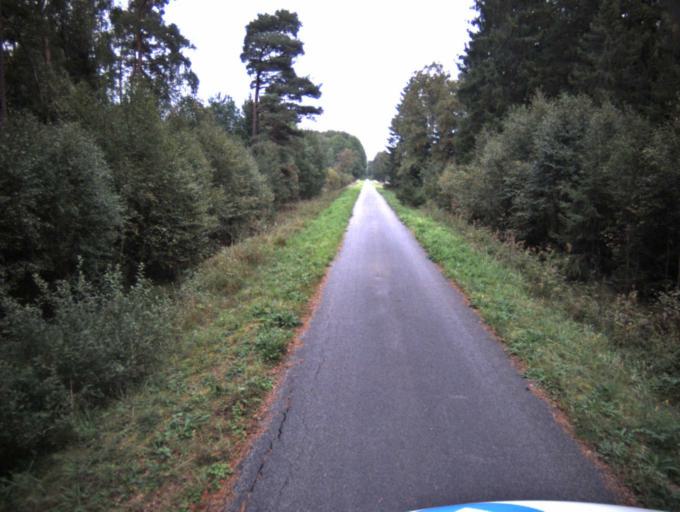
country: SE
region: Vaestra Goetaland
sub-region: Ulricehamns Kommun
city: Ulricehamn
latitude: 57.9482
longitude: 13.5030
